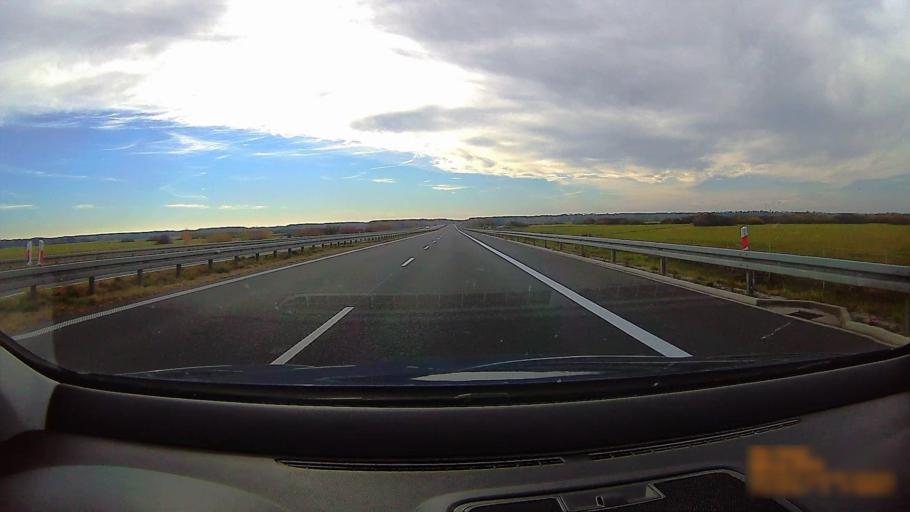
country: PL
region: Greater Poland Voivodeship
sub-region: Powiat ostrowski
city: Przygodzice
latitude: 51.5877
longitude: 17.8497
